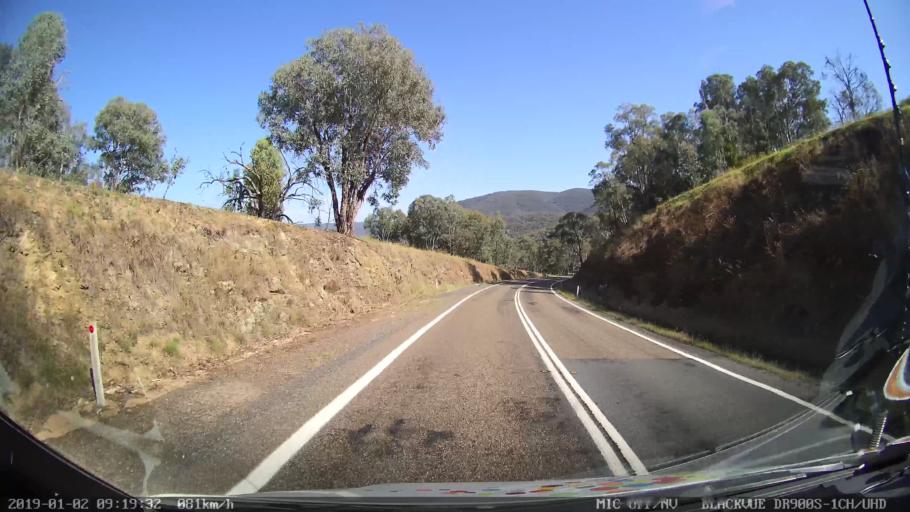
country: AU
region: New South Wales
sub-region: Tumut Shire
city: Tumut
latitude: -35.4213
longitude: 148.2773
